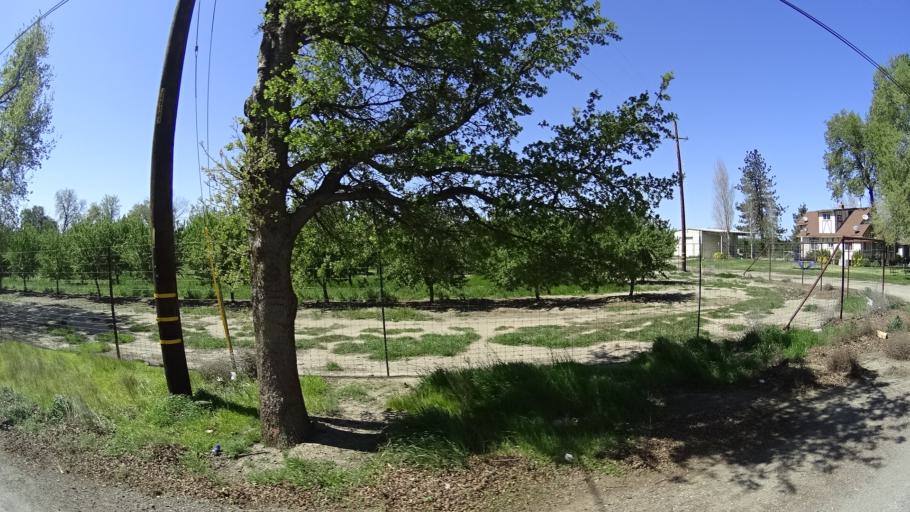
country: US
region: California
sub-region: Glenn County
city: Orland
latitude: 39.7736
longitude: -122.2478
